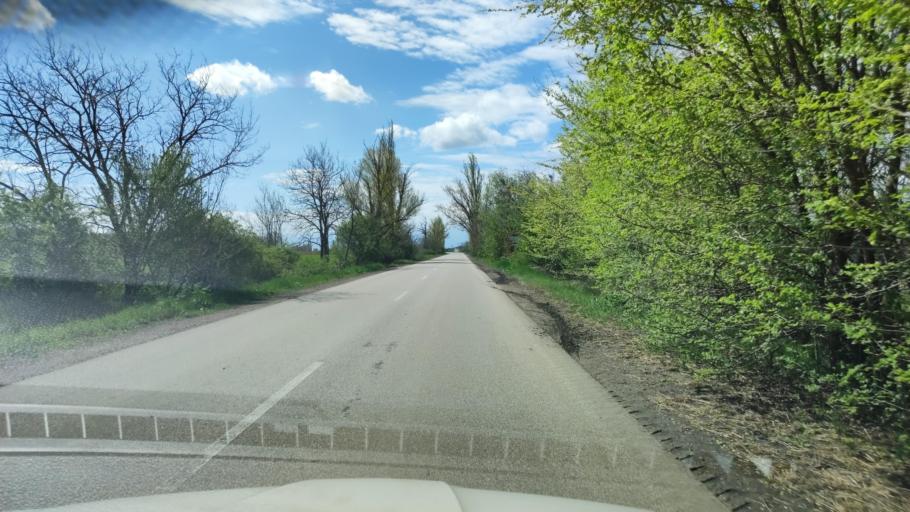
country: HU
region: Pest
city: Abony
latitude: 47.1707
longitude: 20.0041
